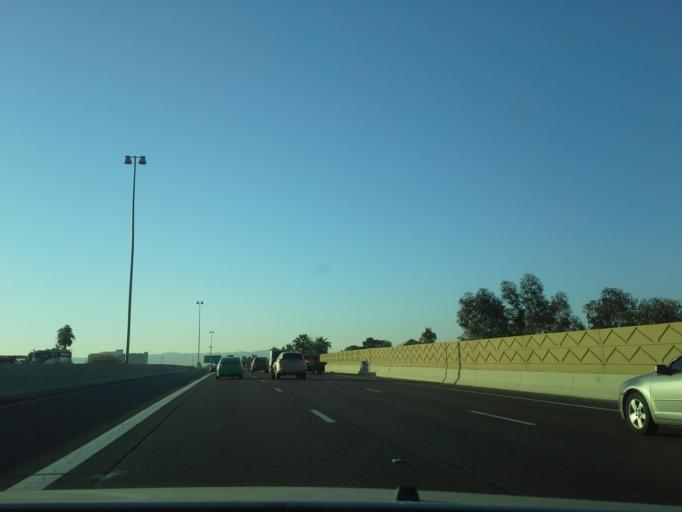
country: US
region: Arizona
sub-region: Maricopa County
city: Phoenix
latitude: 33.4958
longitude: -112.0439
